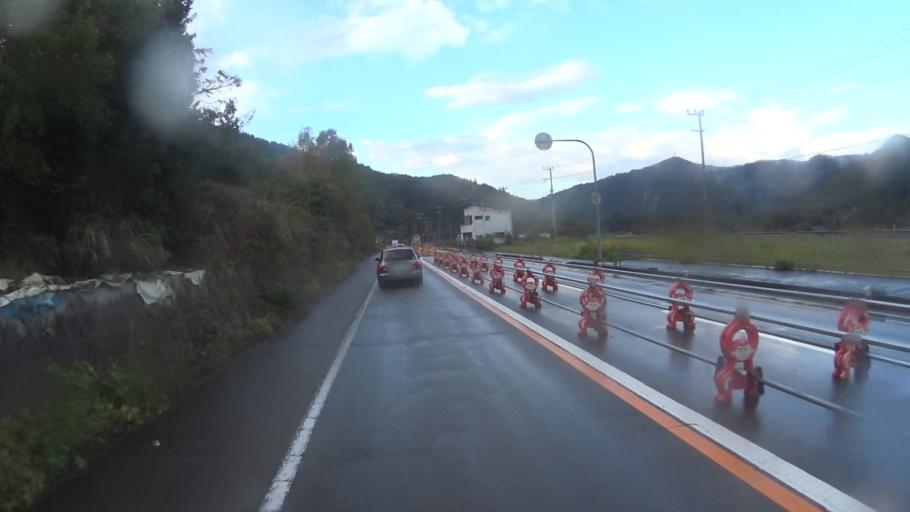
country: JP
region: Kyoto
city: Ayabe
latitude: 35.2076
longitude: 135.2683
